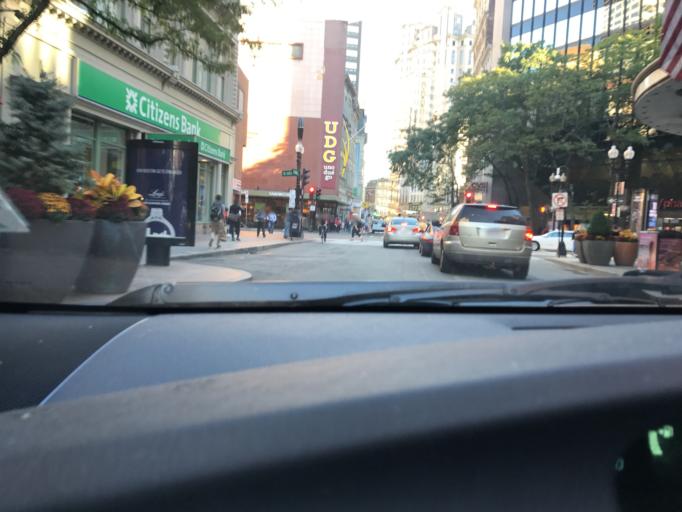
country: US
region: Massachusetts
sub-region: Suffolk County
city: Boston
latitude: 42.3548
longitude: -71.0595
